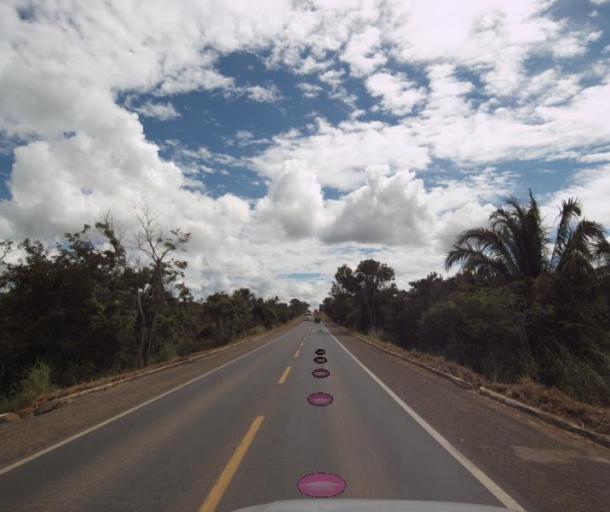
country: BR
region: Goias
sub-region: Uruacu
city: Uruacu
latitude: -14.4445
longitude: -49.1566
